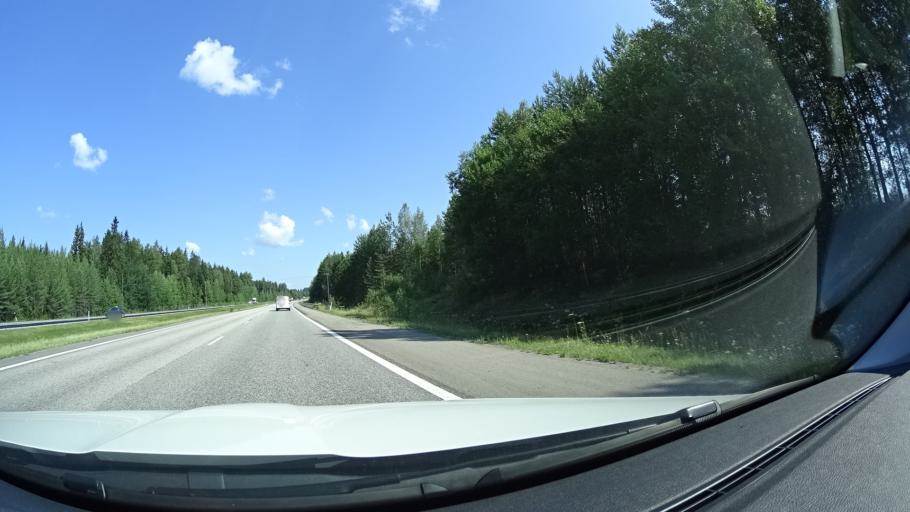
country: FI
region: Uusimaa
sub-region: Helsinki
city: Nurmijaervi
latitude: 60.4278
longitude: 24.8273
